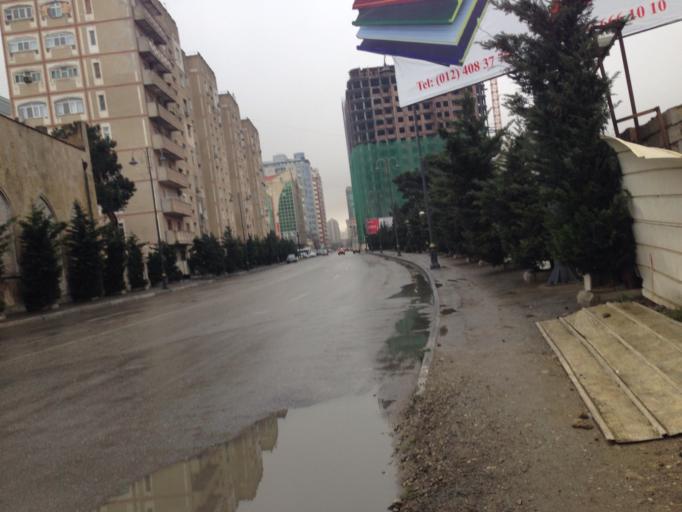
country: AZ
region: Baki
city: Baku
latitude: 40.3994
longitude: 49.8445
